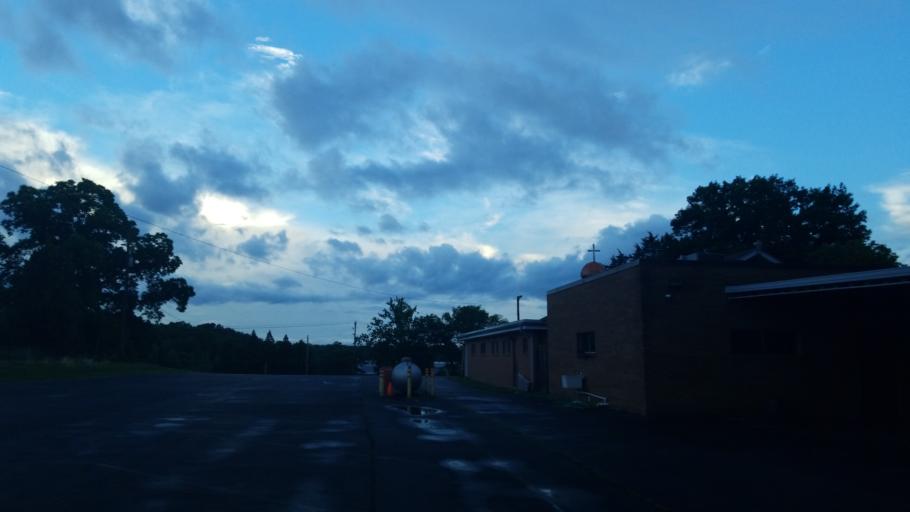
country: US
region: Tennessee
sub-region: Rutherford County
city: La Vergne
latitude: 36.1145
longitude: -86.6417
